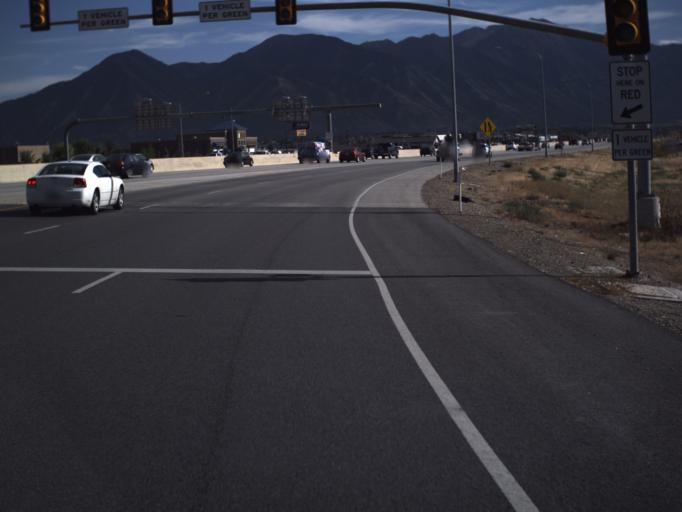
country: US
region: Utah
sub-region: Utah County
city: Springville
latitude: 40.1597
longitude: -111.6473
